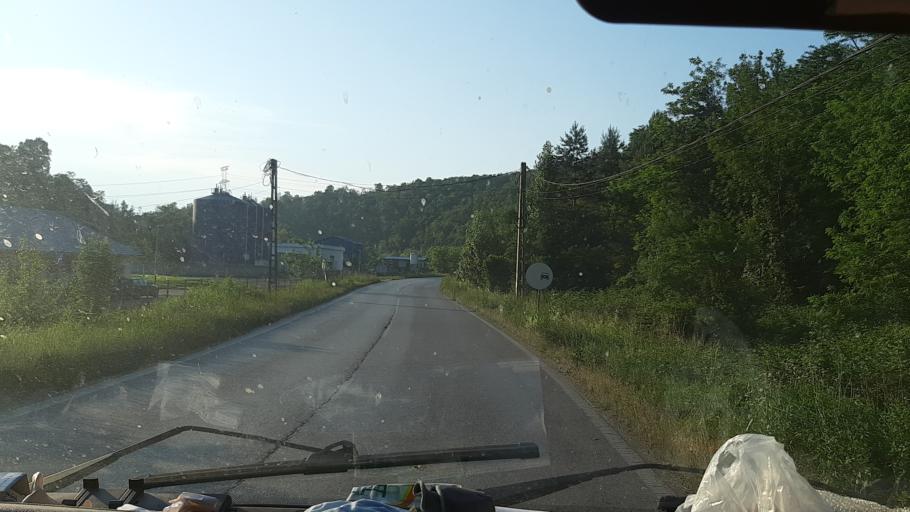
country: RO
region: Caras-Severin
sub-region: Municipiul Resita
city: Calnic
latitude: 45.3412
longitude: 21.8442
